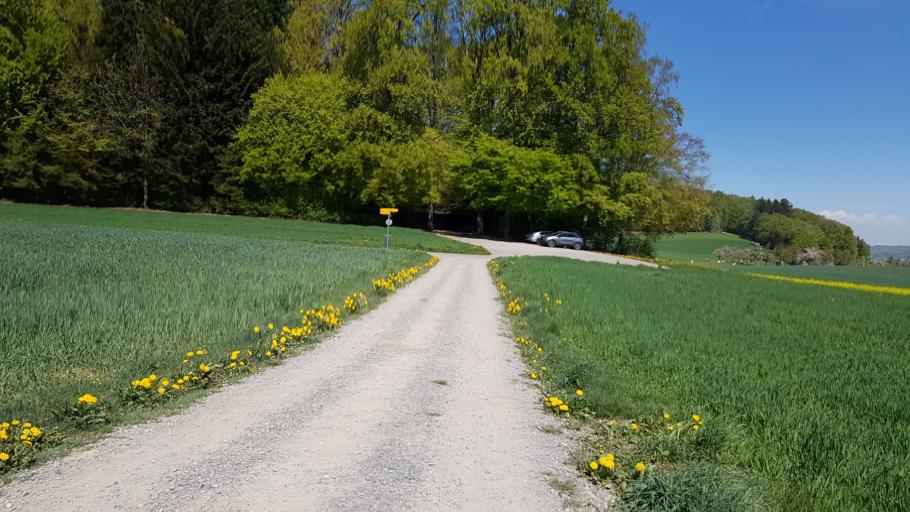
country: CH
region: Aargau
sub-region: Bezirk Lenzburg
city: Boniswil
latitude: 47.2891
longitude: 8.1876
